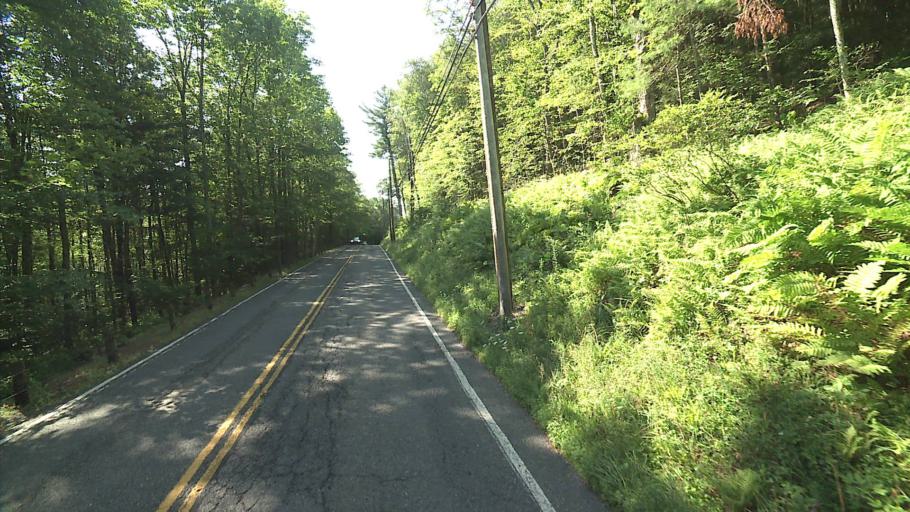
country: US
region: Connecticut
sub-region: Litchfield County
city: Winsted
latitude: 41.9977
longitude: -73.1010
